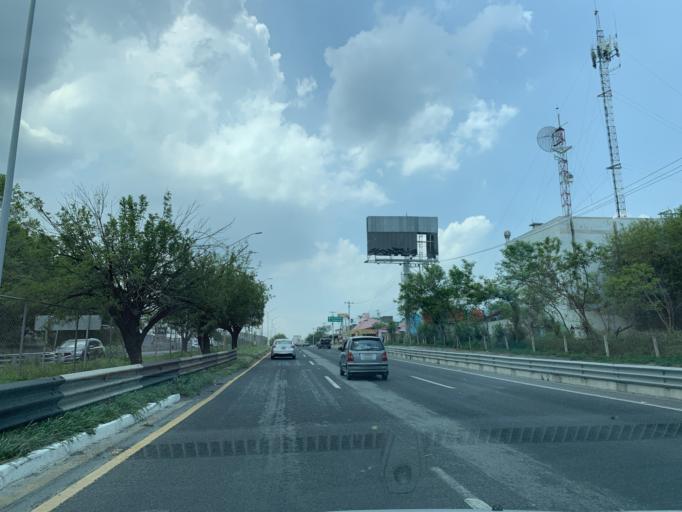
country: MX
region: Nuevo Leon
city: Santiago
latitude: 25.4937
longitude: -100.1871
